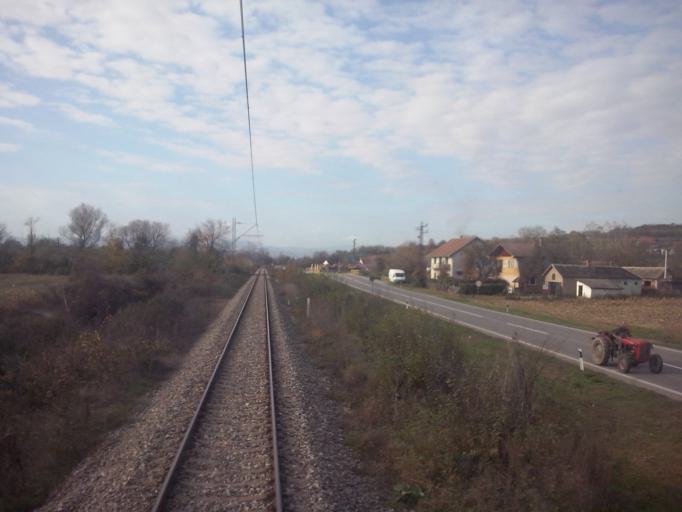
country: RS
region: Central Serbia
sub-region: Kolubarski Okrug
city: Mionica
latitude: 44.3097
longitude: 20.0583
